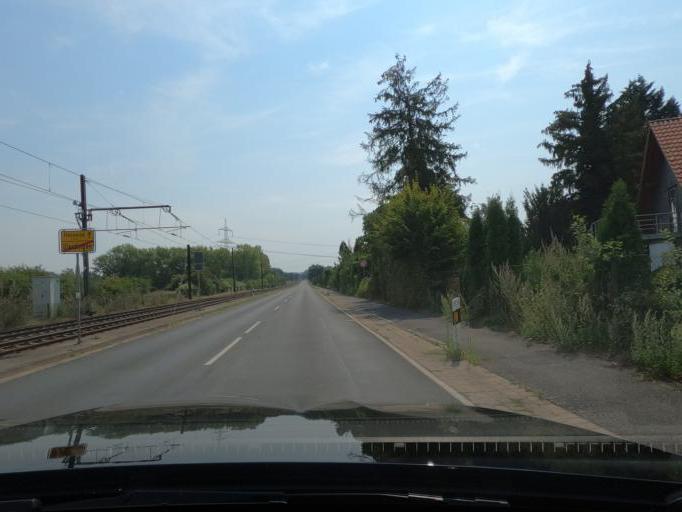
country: DE
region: Lower Saxony
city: Sarstedt
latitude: 52.2680
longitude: 9.8426
